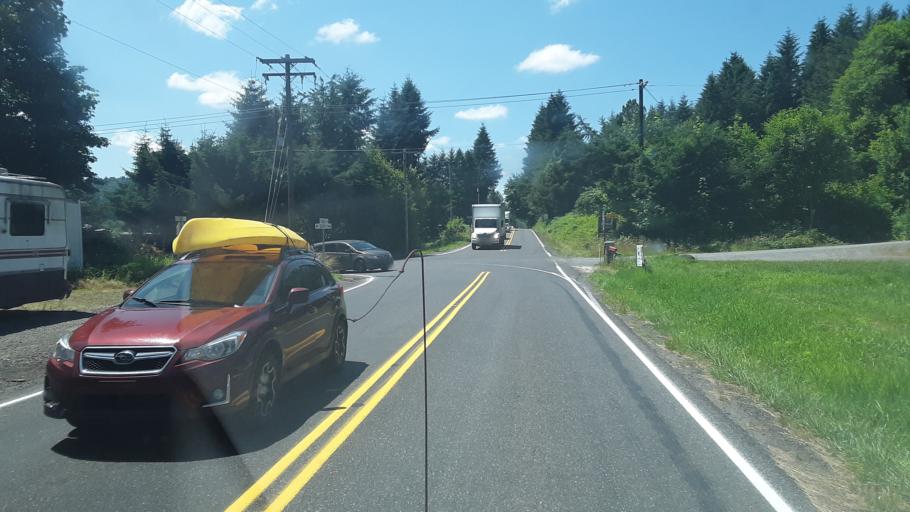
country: US
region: Washington
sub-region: Clark County
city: Amboy
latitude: 45.9173
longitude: -122.4462
